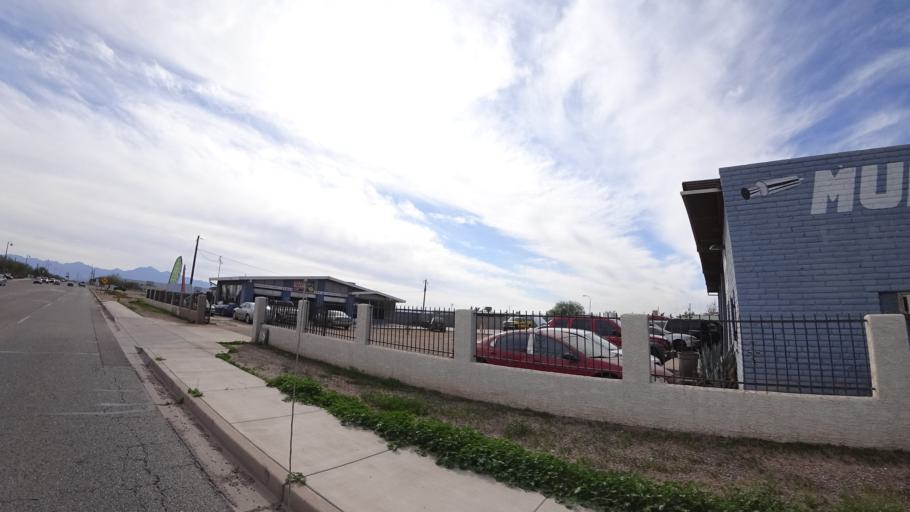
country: US
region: Arizona
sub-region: Maricopa County
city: Tolleson
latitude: 33.4456
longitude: -112.2552
